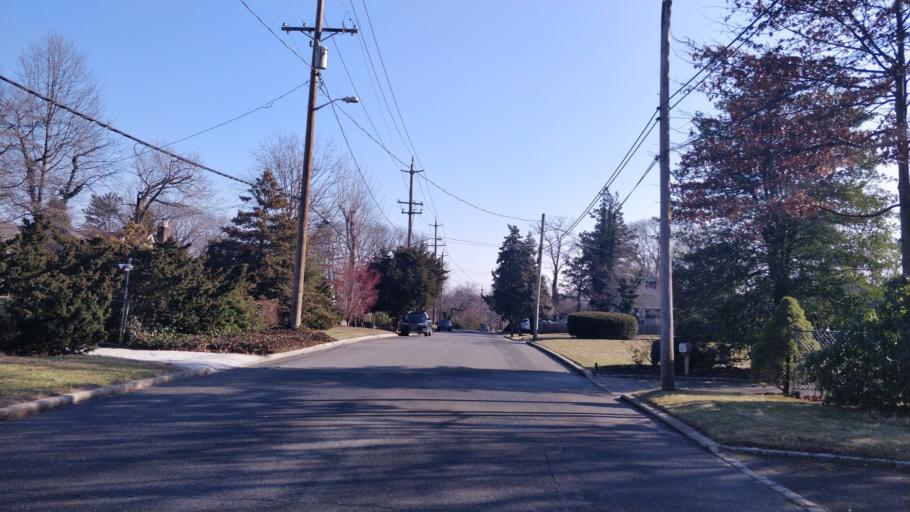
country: US
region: New York
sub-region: Nassau County
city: Glen Cove
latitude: 40.8583
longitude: -73.6280
